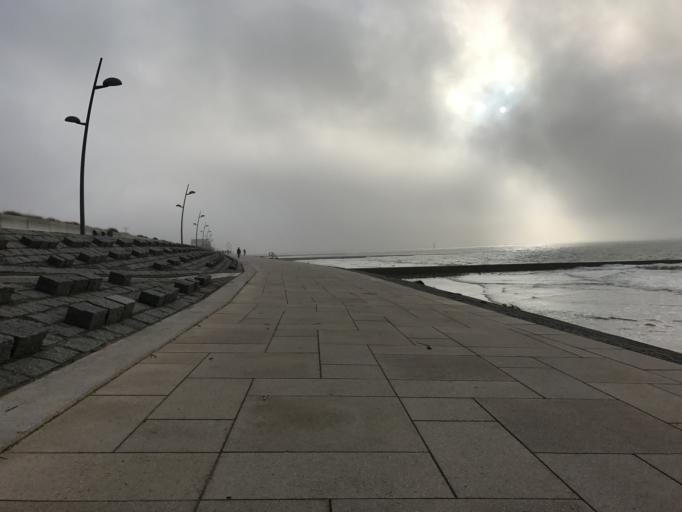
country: DE
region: Lower Saxony
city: Borkum
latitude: 53.5835
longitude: 6.6582
